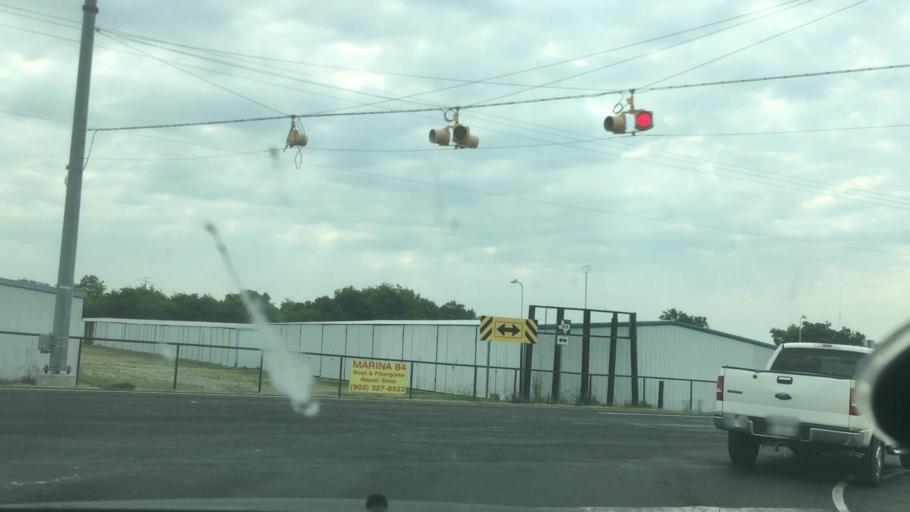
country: US
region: Texas
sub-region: Grayson County
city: Pottsboro
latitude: 33.7963
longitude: -96.6121
